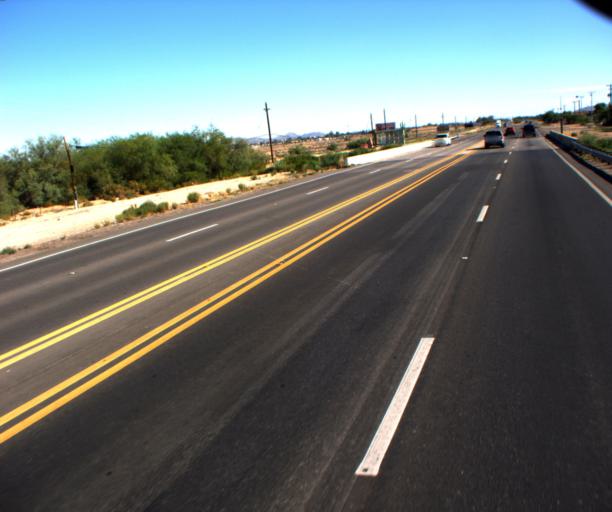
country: US
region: Arizona
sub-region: Pinal County
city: Casa Grande
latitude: 32.9158
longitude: -111.7570
